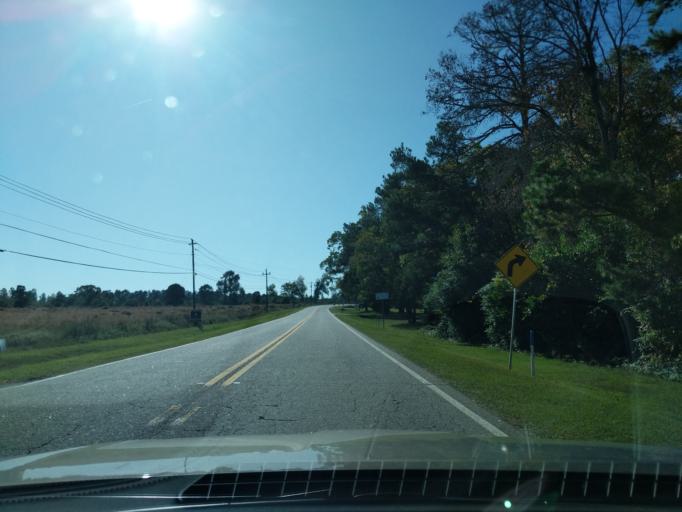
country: US
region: Georgia
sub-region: Columbia County
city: Grovetown
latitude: 33.4681
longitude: -82.1582
